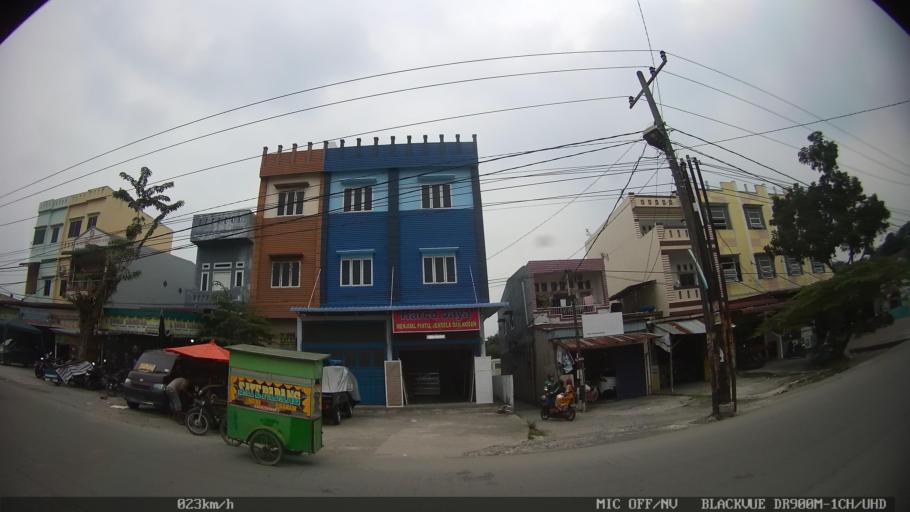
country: ID
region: North Sumatra
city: Medan
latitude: 3.5813
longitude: 98.7261
